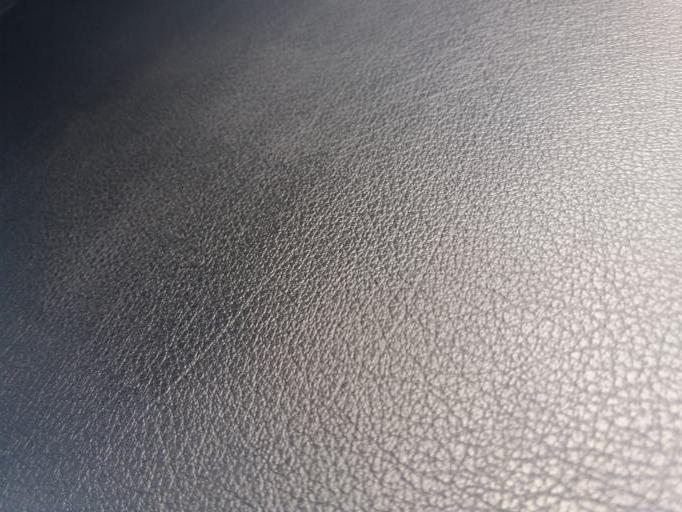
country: MX
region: Aguascalientes
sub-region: Aguascalientes
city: San Sebastian [Fraccionamiento]
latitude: 21.8105
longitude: -102.3044
